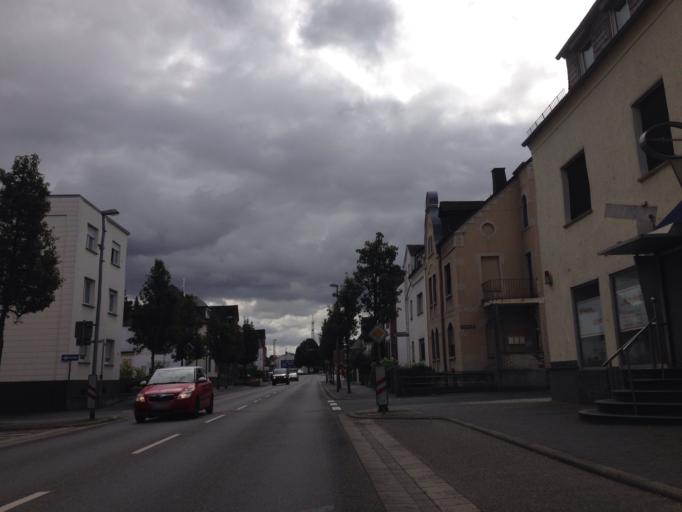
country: DE
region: Hesse
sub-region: Regierungsbezirk Giessen
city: Elz
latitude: 50.4083
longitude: 8.0360
